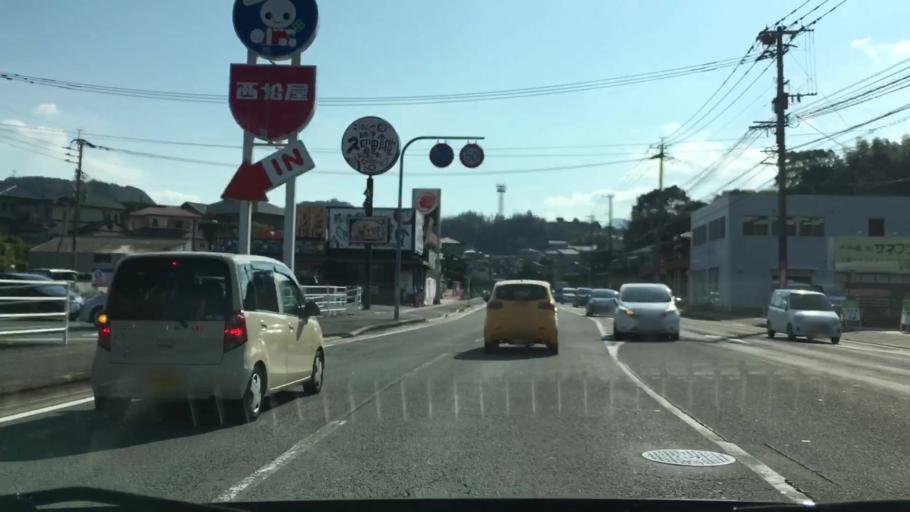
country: JP
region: Nagasaki
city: Togitsu
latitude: 32.8388
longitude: 129.8378
